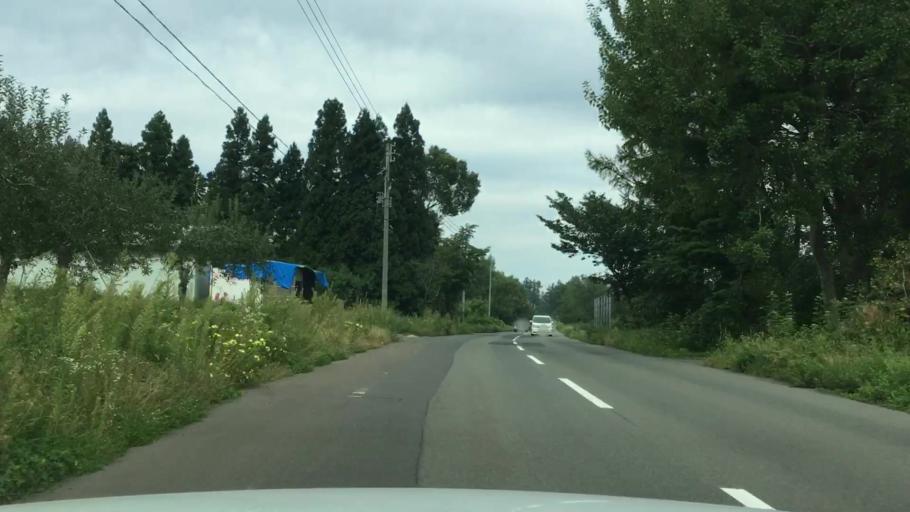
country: JP
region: Aomori
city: Hirosaki
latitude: 40.6809
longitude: 140.3713
